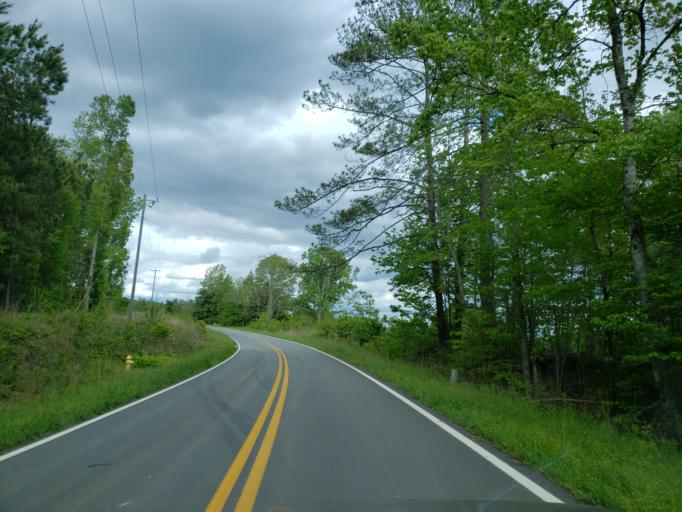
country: US
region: Georgia
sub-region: Haralson County
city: Tallapoosa
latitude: 33.8633
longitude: -85.3204
